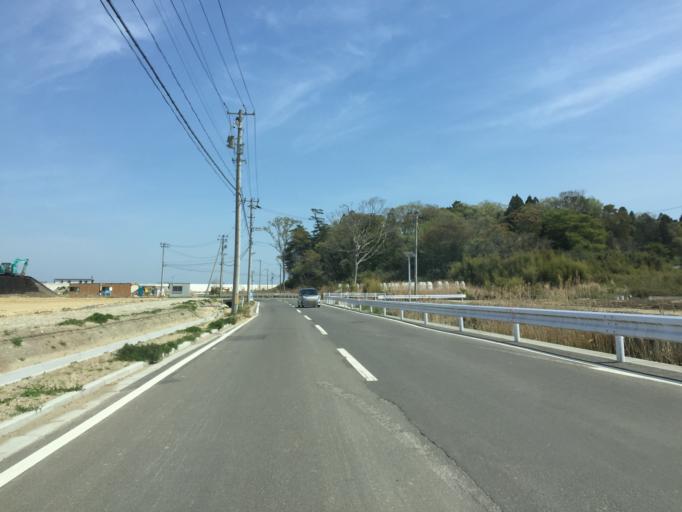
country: JP
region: Miyagi
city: Watari
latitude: 37.8999
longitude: 140.9247
